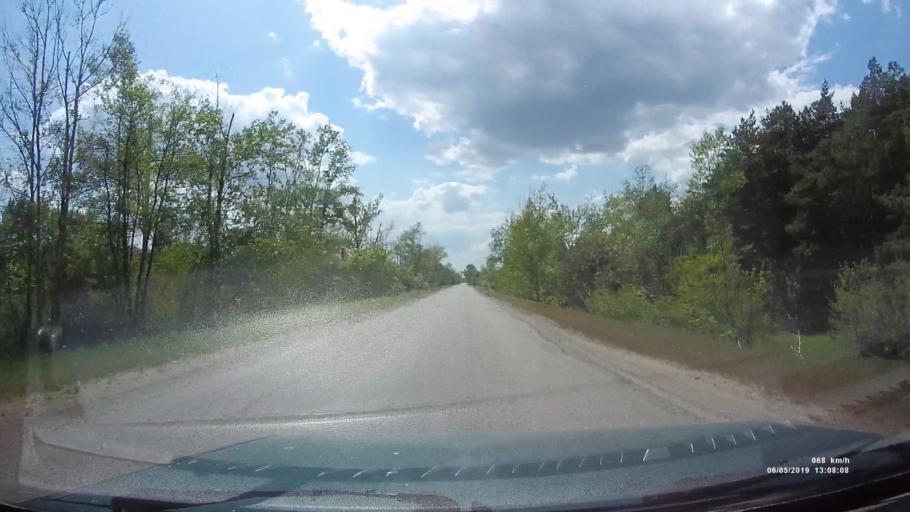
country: RU
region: Rostov
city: Ust'-Donetskiy
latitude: 47.7775
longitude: 40.9985
